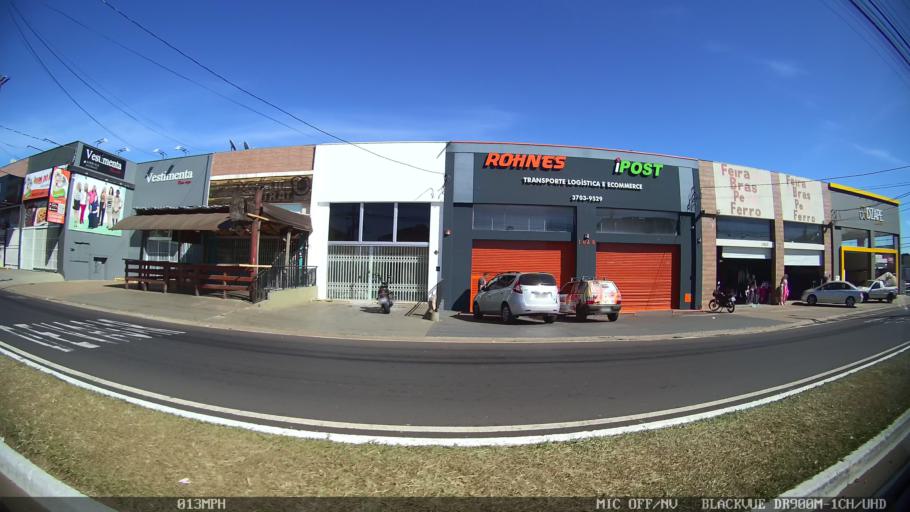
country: BR
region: Sao Paulo
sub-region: Franca
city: Franca
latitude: -20.5238
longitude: -47.3703
